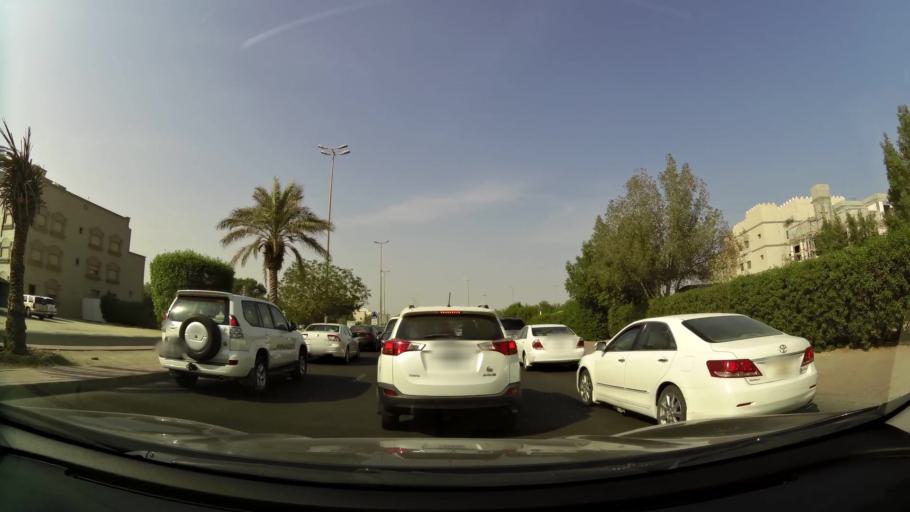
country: KW
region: Mubarak al Kabir
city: Mubarak al Kabir
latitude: 29.1735
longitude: 48.0848
